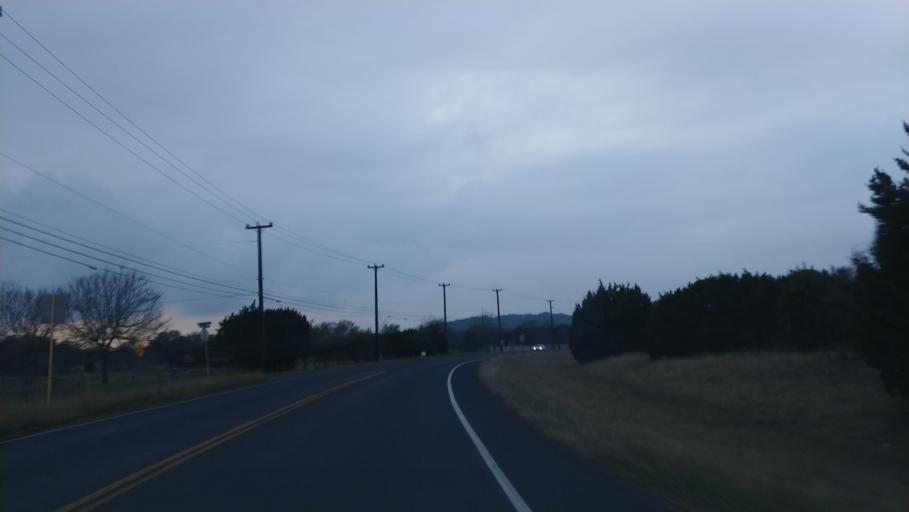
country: US
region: Texas
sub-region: Bexar County
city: Cross Mountain
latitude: 29.6775
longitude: -98.6643
